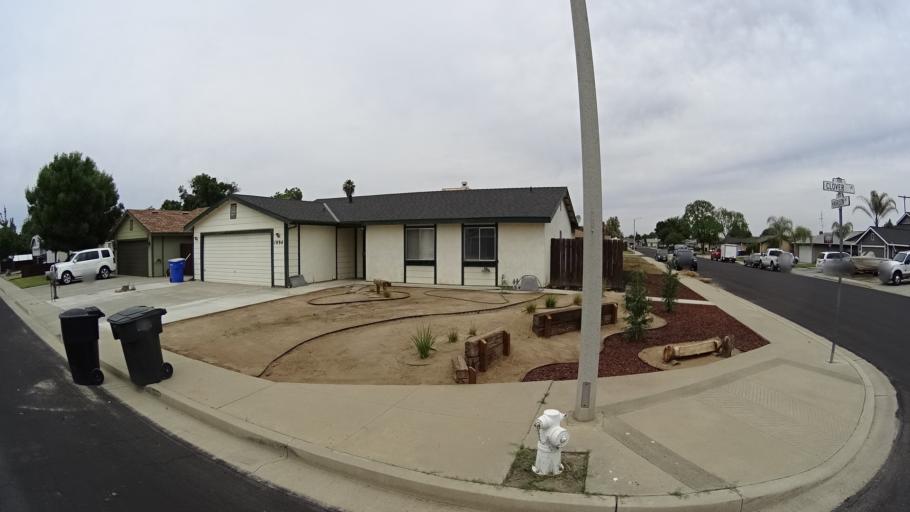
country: US
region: California
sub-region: Kings County
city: Hanford
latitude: 36.3475
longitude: -119.6286
